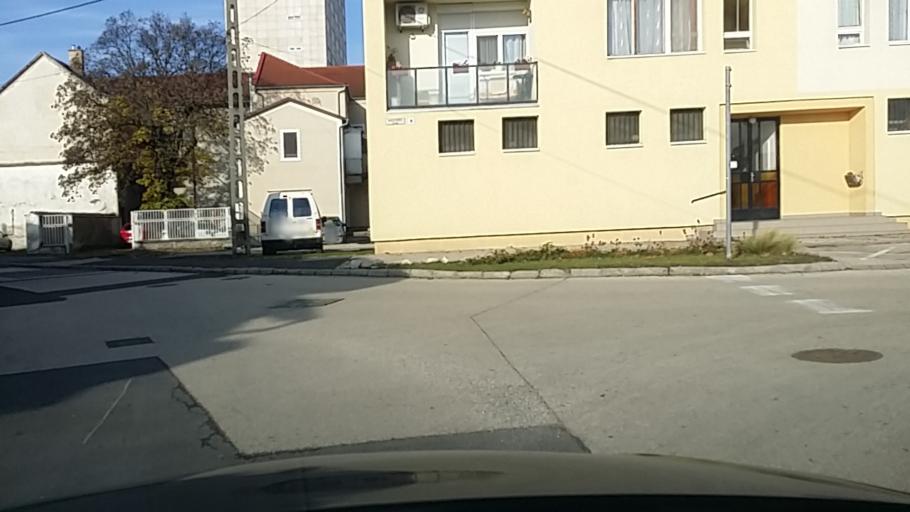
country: HU
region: Veszprem
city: Tapolca
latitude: 46.8816
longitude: 17.4369
